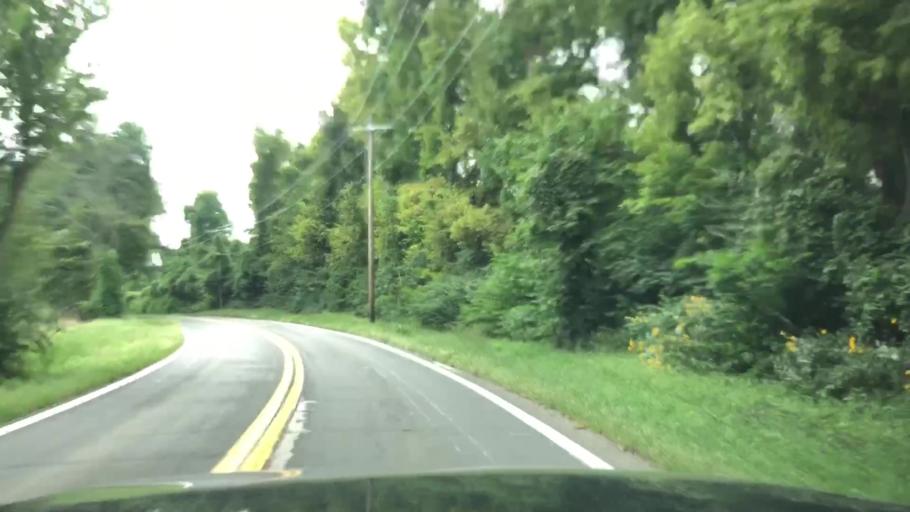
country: US
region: Missouri
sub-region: Saint Louis County
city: Hazelwood
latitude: 38.8153
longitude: -90.3769
